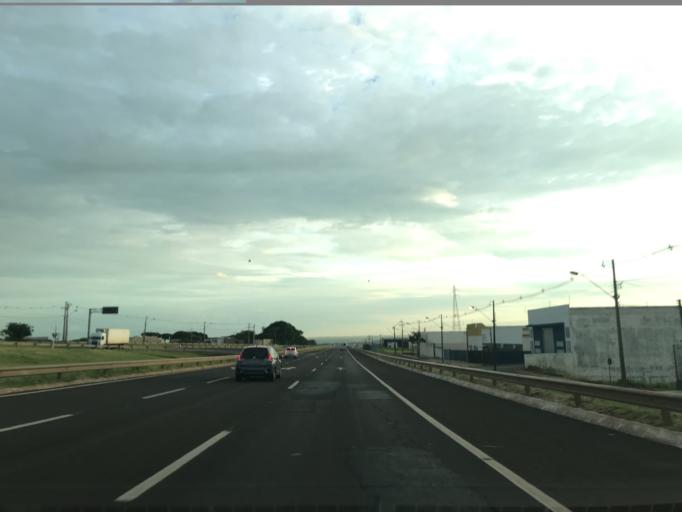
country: BR
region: Parana
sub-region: Maringa
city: Maringa
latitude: -23.4043
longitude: -51.9823
